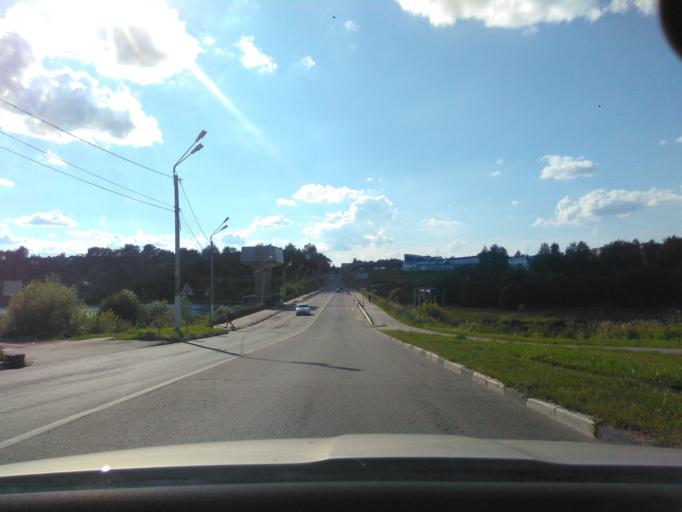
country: RU
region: Moskovskaya
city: Klin
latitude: 56.3178
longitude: 36.7390
